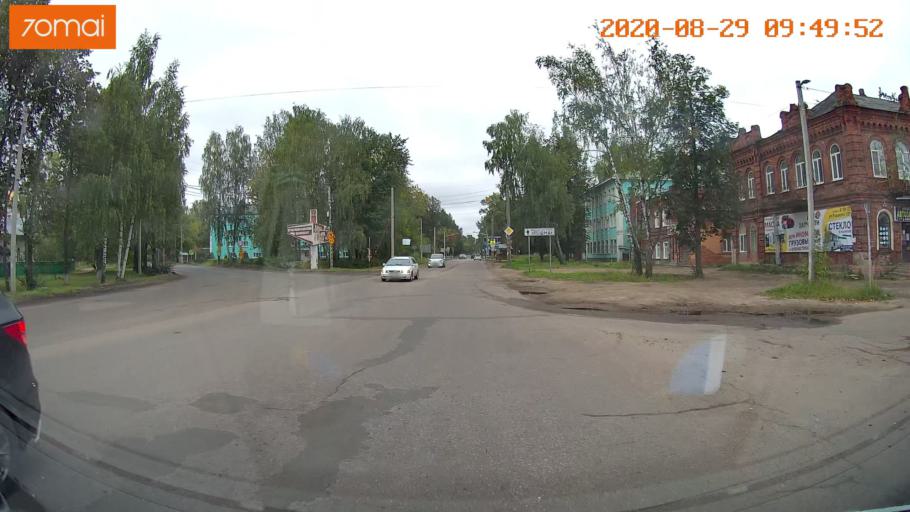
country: RU
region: Ivanovo
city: Kineshma
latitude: 57.4390
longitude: 42.1878
